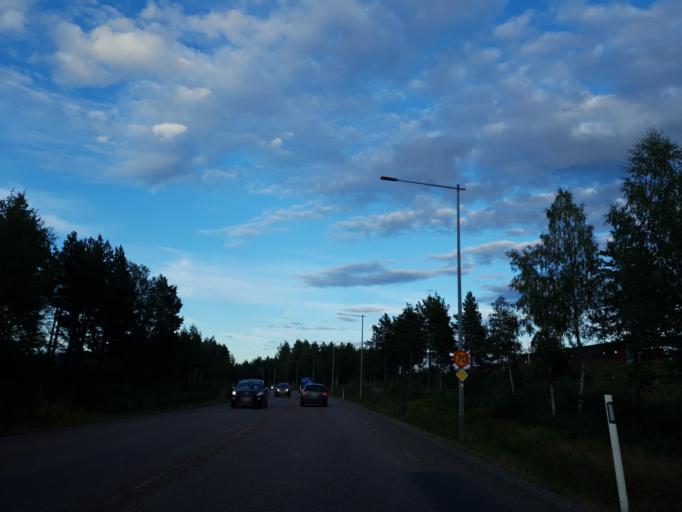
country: SE
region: Gaevleborg
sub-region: Soderhamns Kommun
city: Soderhamn
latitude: 61.2912
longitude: 17.0634
